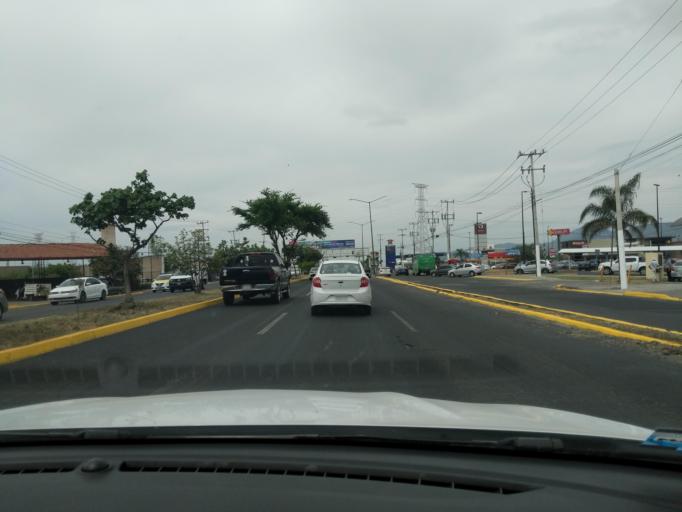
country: MX
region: Jalisco
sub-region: Zapopan
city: La Cuchilla (Extramuros de Tesistan)
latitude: 20.7757
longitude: -103.4548
